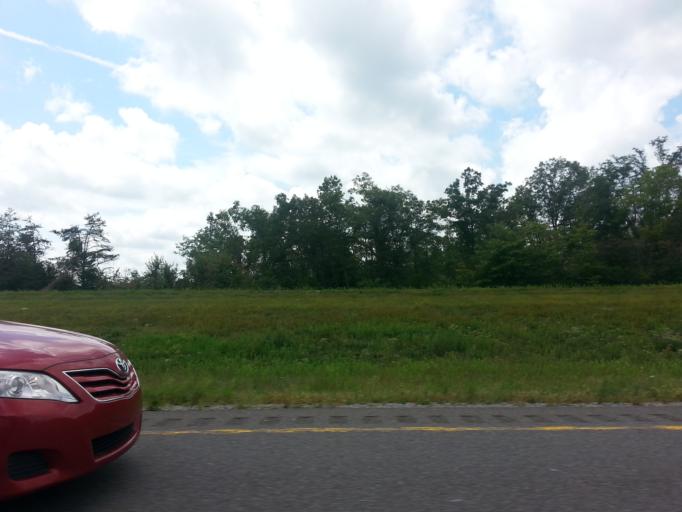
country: US
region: Tennessee
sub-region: Cumberland County
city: Crossville
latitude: 36.0403
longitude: -85.1102
